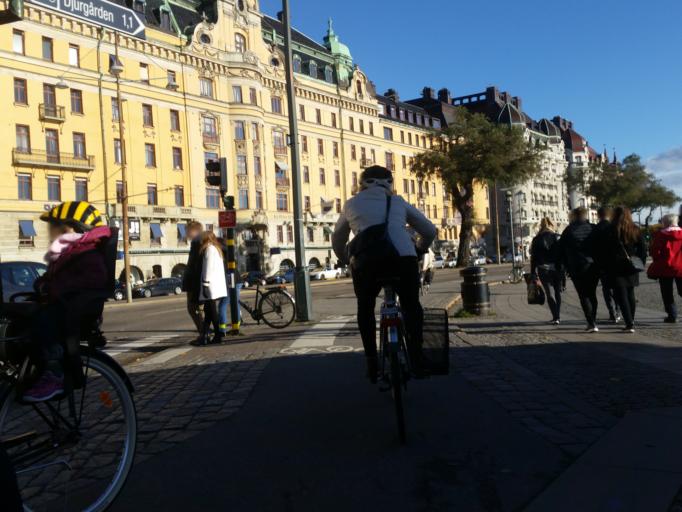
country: SE
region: Stockholm
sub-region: Stockholms Kommun
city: OEstermalm
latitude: 59.3323
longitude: 18.0771
